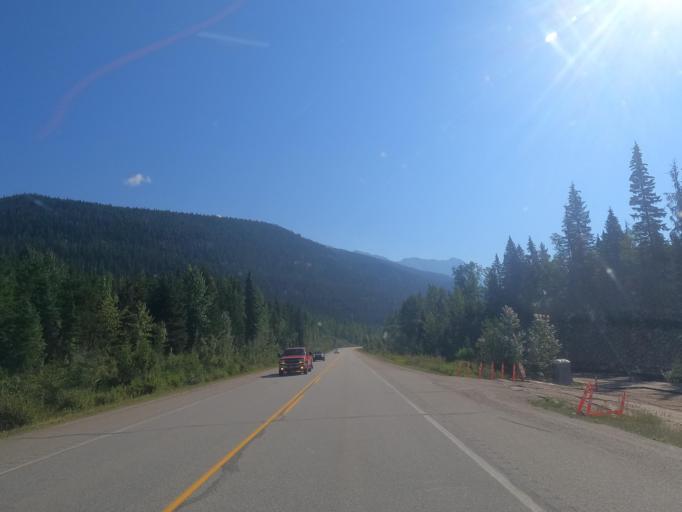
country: CA
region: Alberta
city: Jasper Park Lodge
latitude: 52.8926
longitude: -118.7406
